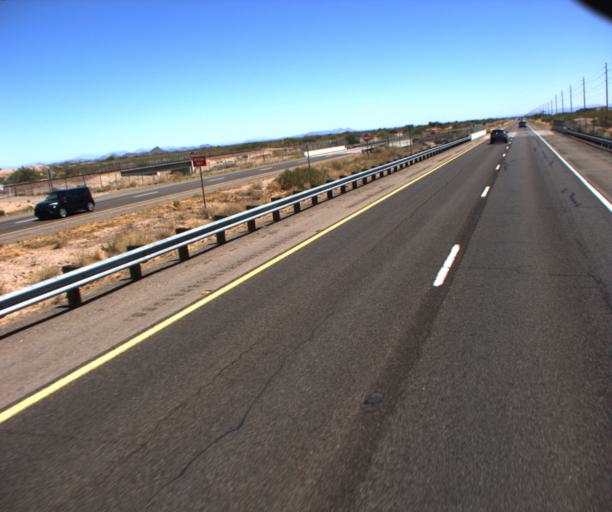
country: US
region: Arizona
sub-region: Maricopa County
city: Sun City West
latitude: 33.7461
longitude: -112.4882
